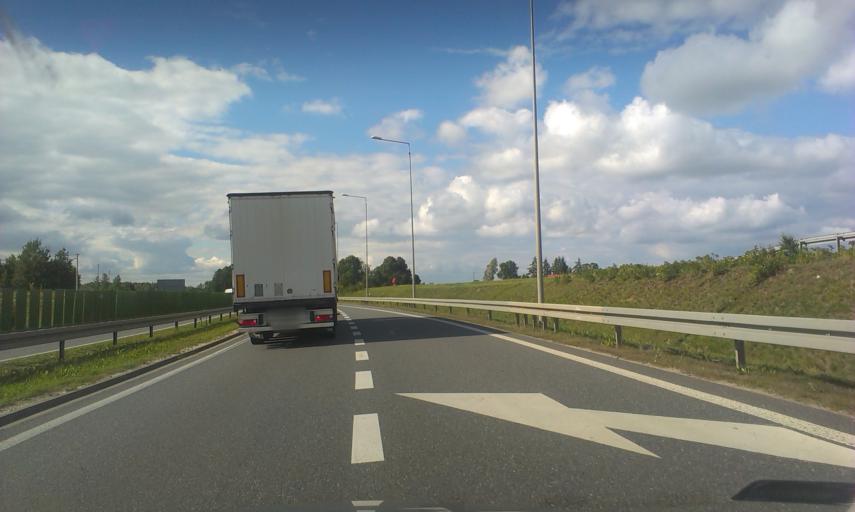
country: PL
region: Masovian Voivodeship
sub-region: Powiat zyrardowski
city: Radziejowice
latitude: 51.9732
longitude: 20.5719
